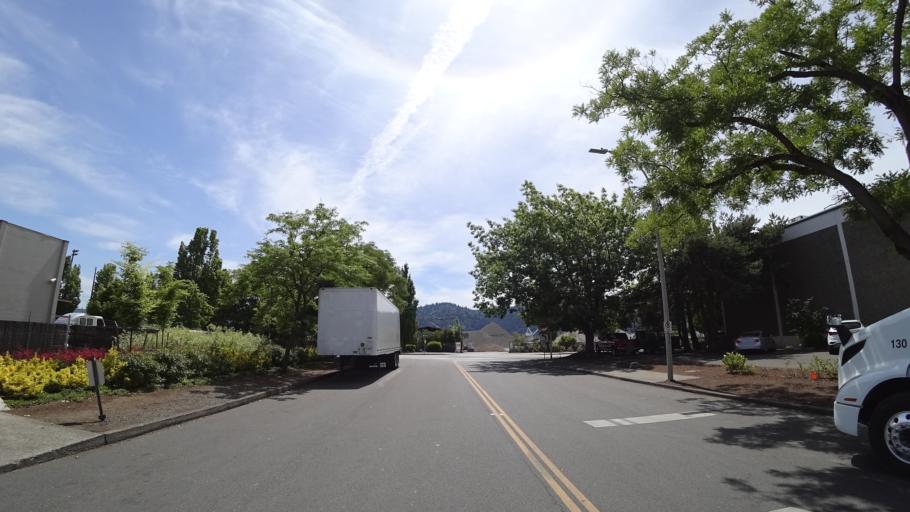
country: US
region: Oregon
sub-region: Multnomah County
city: Portland
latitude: 45.5607
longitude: -122.7113
